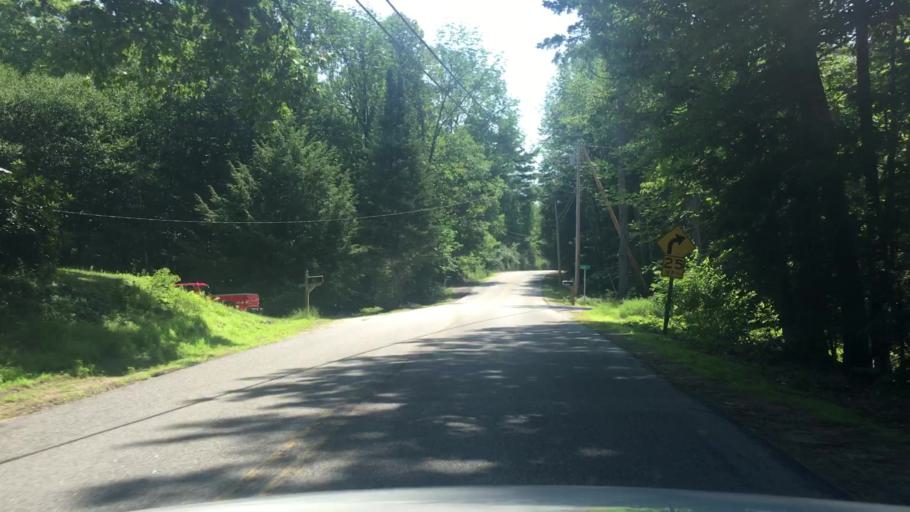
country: US
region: Maine
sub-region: Cumberland County
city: Cumberland Center
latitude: 43.8500
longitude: -70.3134
